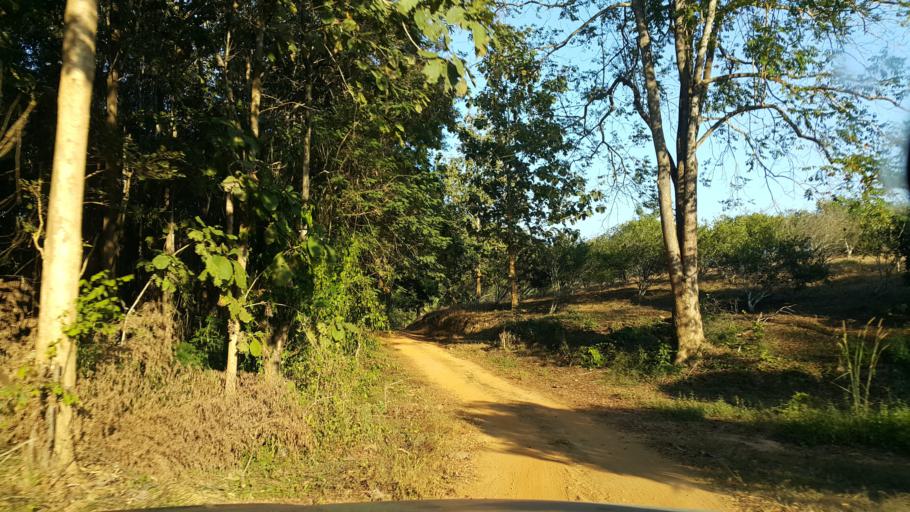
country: TH
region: Sukhothai
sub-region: Amphoe Si Satchanalai
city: Si Satchanalai
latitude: 17.5841
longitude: 99.6060
